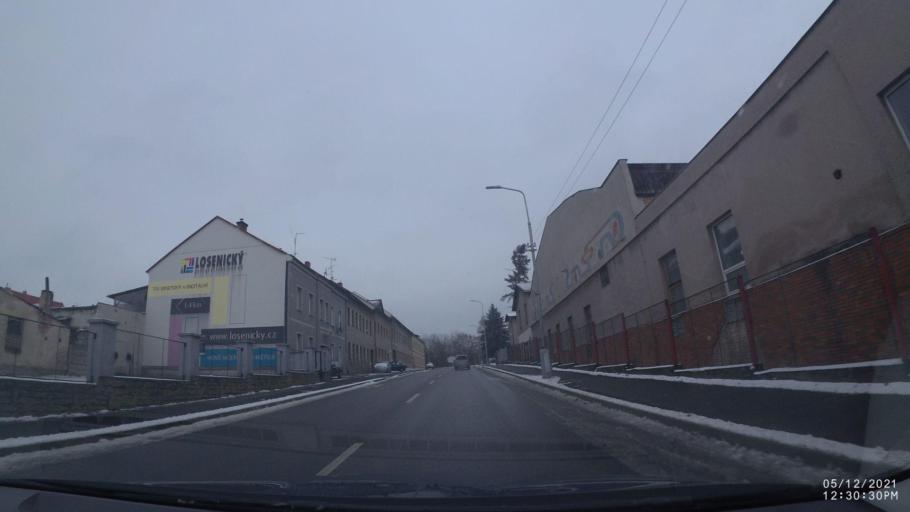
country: CZ
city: Nove Mesto nad Metuji
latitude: 50.3523
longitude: 16.1400
